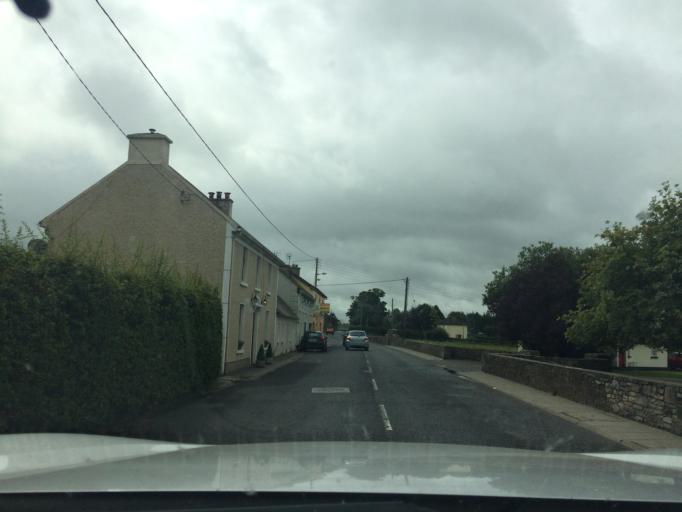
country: IE
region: Munster
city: Thurles
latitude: 52.6371
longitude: -7.8672
